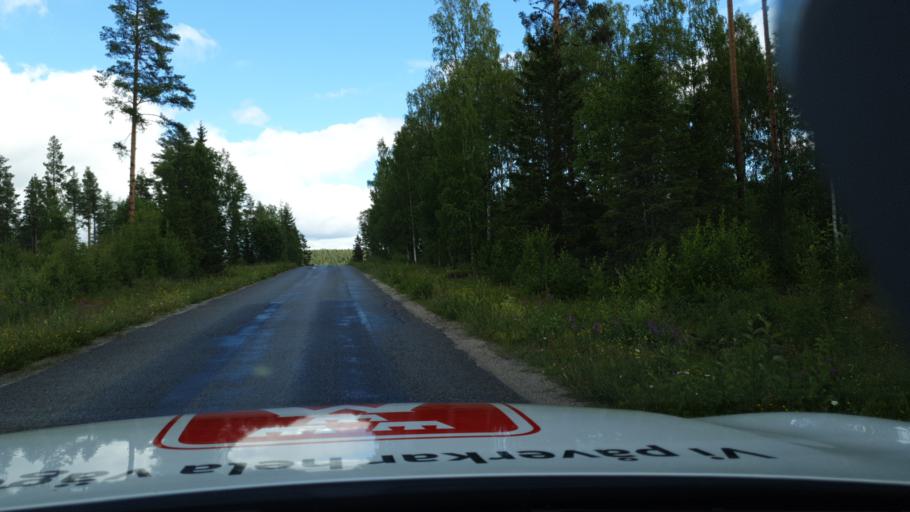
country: SE
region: Jaemtland
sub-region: OEstersunds Kommun
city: Brunflo
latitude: 62.9564
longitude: 15.1049
